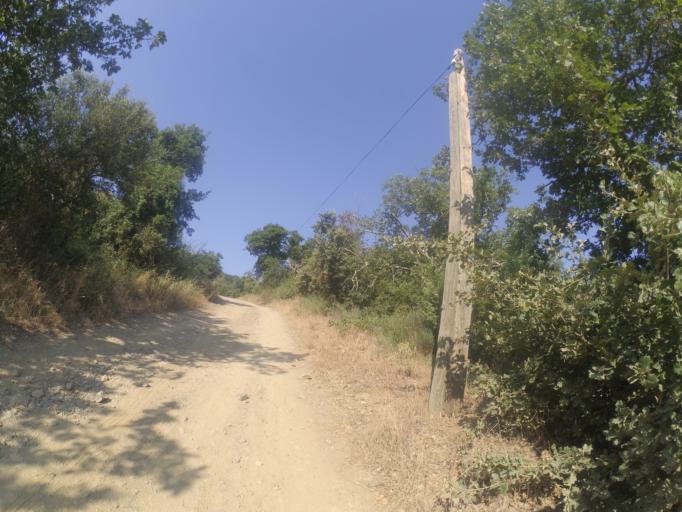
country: FR
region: Languedoc-Roussillon
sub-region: Departement des Pyrenees-Orientales
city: Ille-sur-Tet
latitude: 42.6525
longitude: 2.6559
